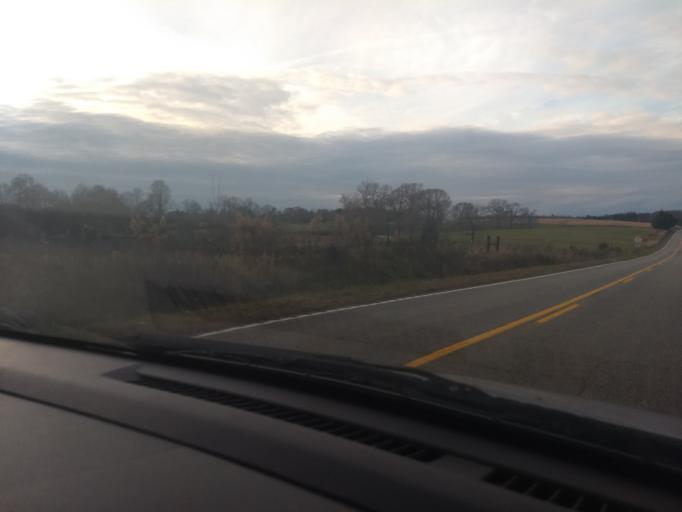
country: US
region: South Carolina
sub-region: Greenville County
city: Greer
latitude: 34.9955
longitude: -82.2076
